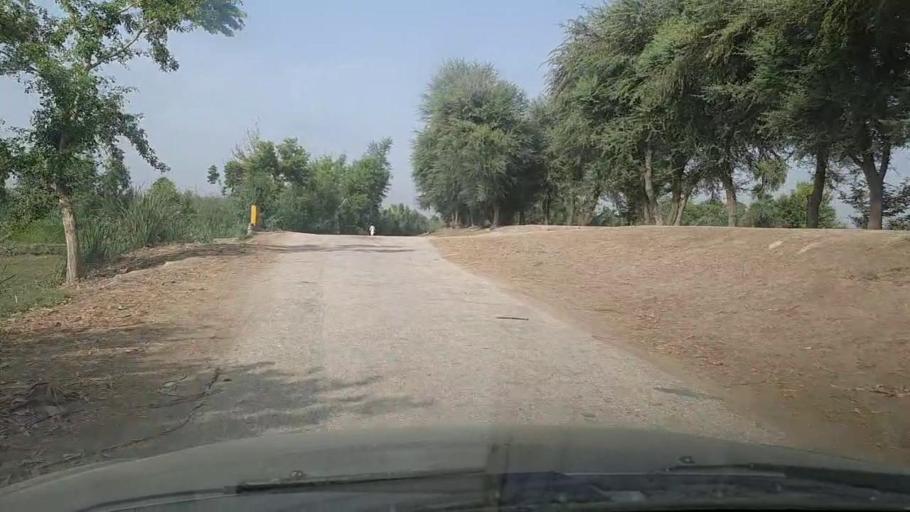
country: PK
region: Sindh
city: Pir jo Goth
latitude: 27.5167
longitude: 68.4771
